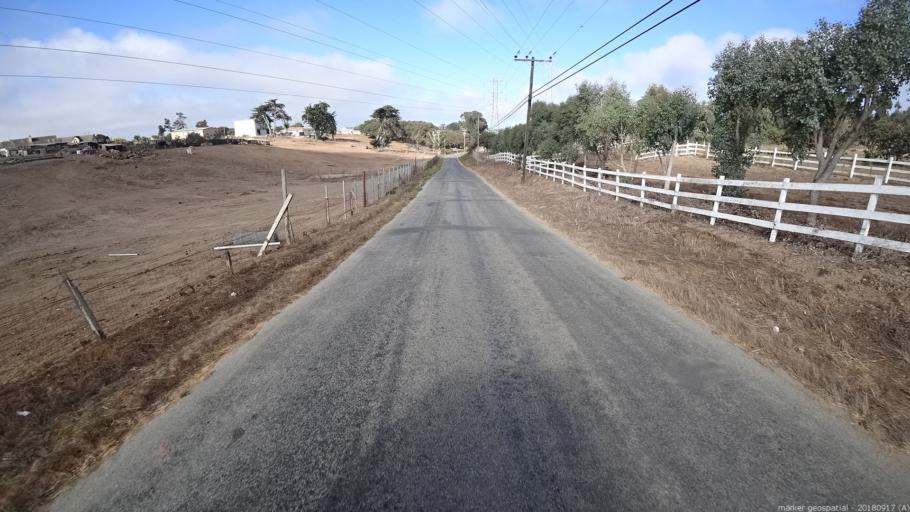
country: US
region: California
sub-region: Monterey County
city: Prunedale
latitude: 36.7913
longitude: -121.7107
